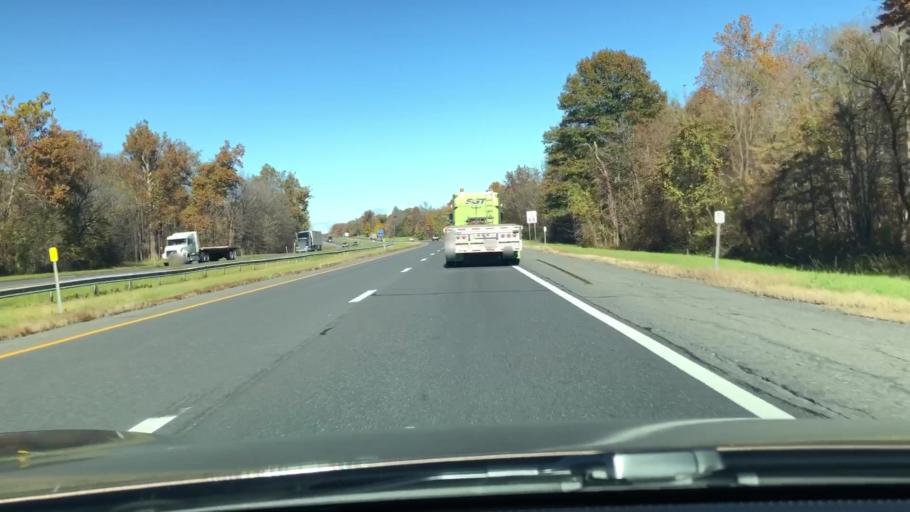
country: US
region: New York
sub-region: Ulster County
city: Lake Katrine
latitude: 42.0284
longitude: -73.9937
